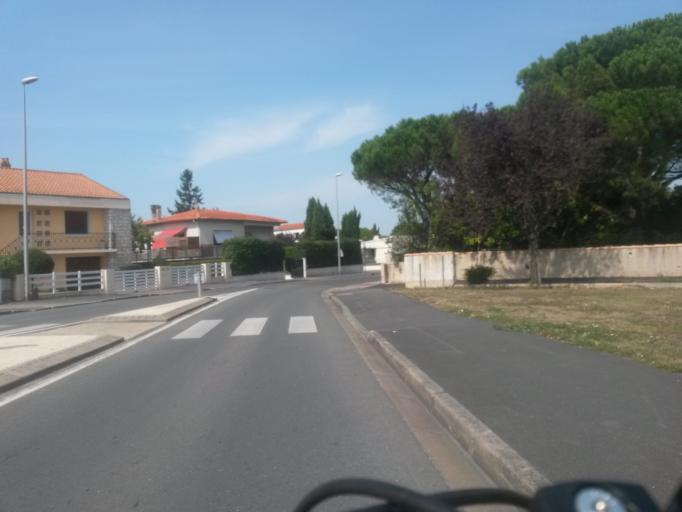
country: FR
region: Poitou-Charentes
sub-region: Departement de la Charente-Maritime
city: Nieul-sur-Mer
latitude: 46.2004
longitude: -1.1603
